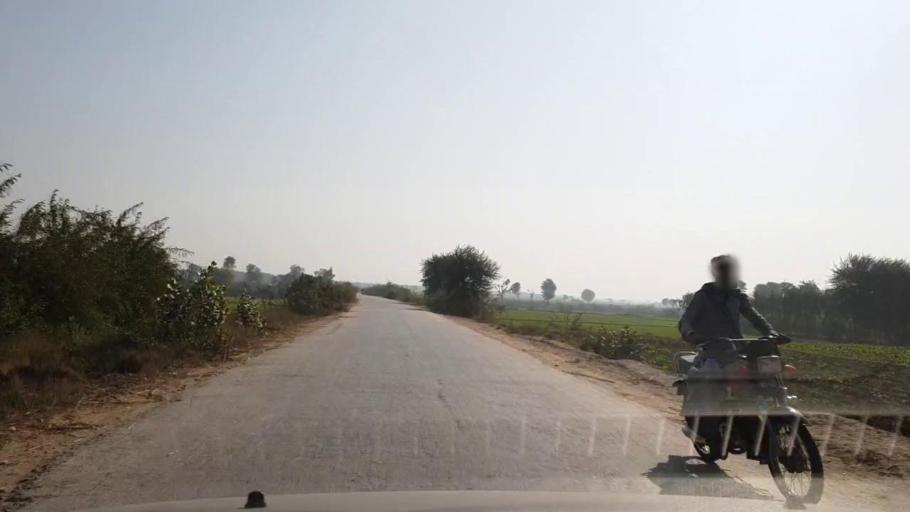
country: PK
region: Sindh
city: Tando Jam
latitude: 25.5214
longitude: 68.5987
